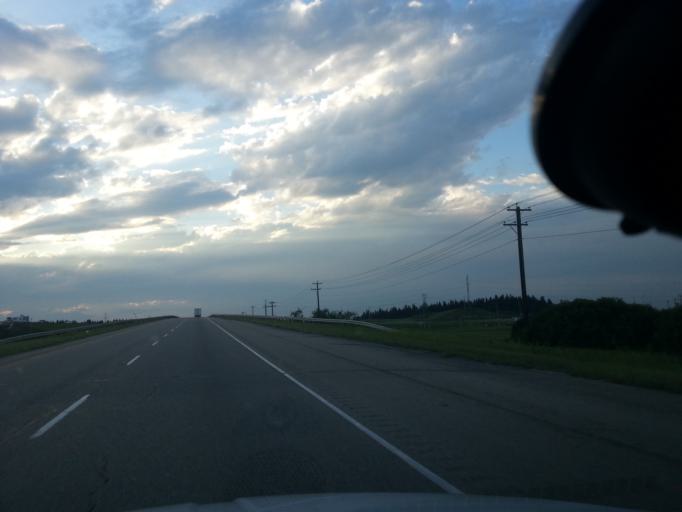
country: CA
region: Alberta
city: Red Deer
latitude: 52.2315
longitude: -113.8201
